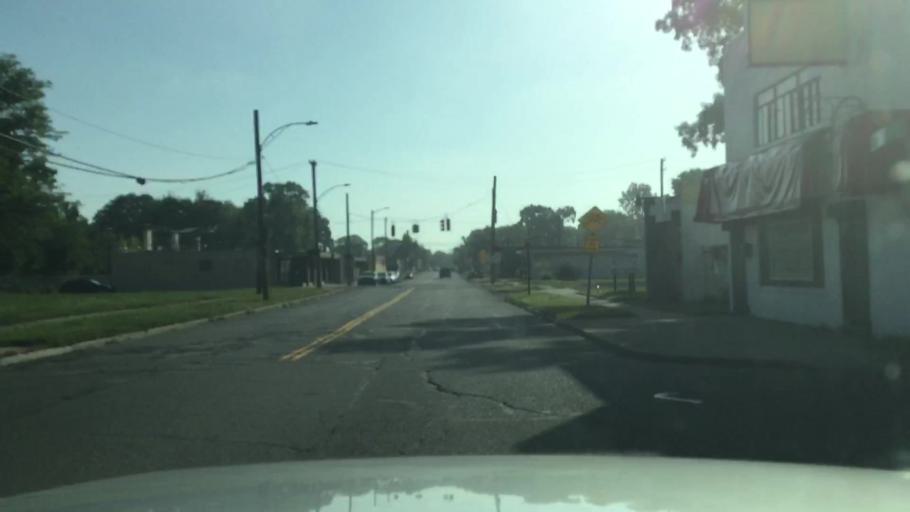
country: US
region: Michigan
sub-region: Oakland County
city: Hazel Park
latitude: 42.4399
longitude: -83.0918
